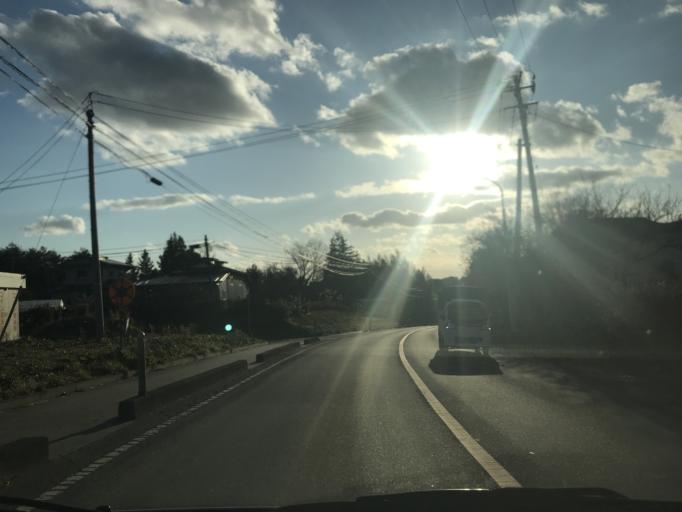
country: JP
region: Miyagi
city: Wakuya
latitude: 38.6823
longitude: 141.1314
